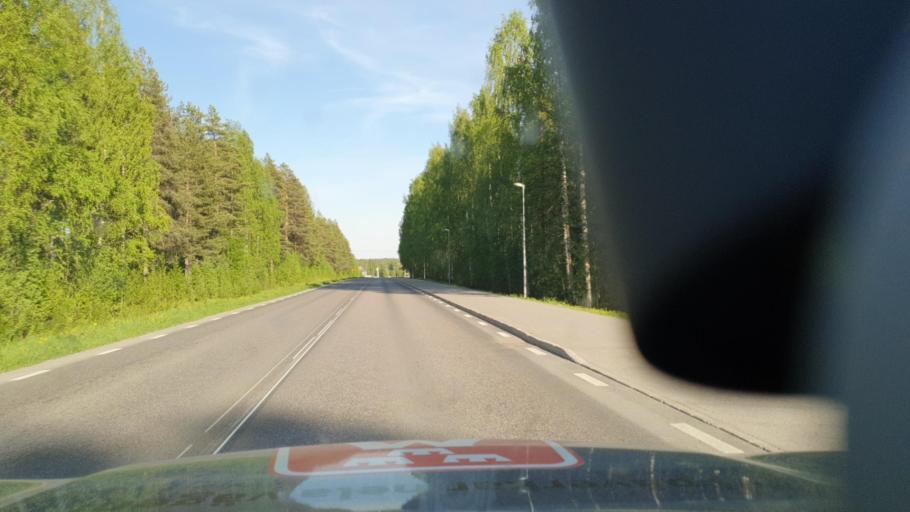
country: SE
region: Norrbotten
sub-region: Bodens Kommun
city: Boden
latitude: 65.8267
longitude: 21.6534
